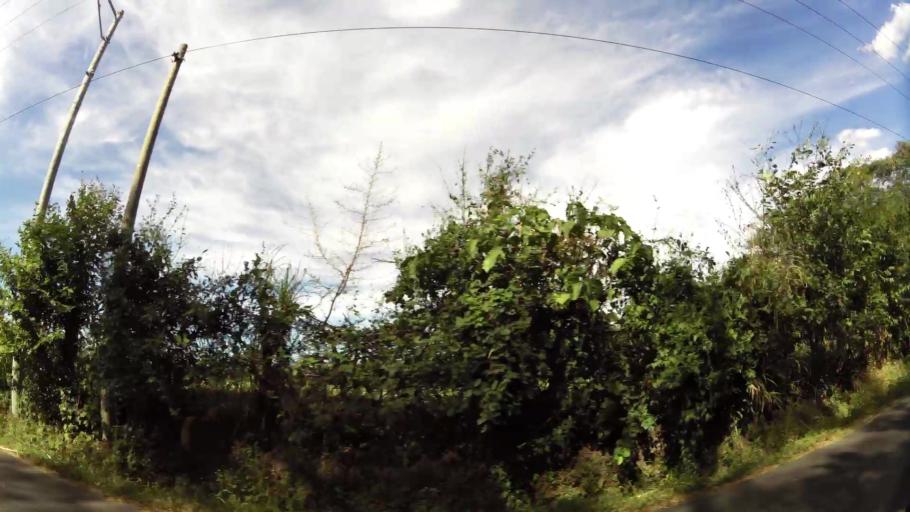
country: SV
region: San Salvador
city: Aguilares
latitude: 13.9603
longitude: -89.1559
